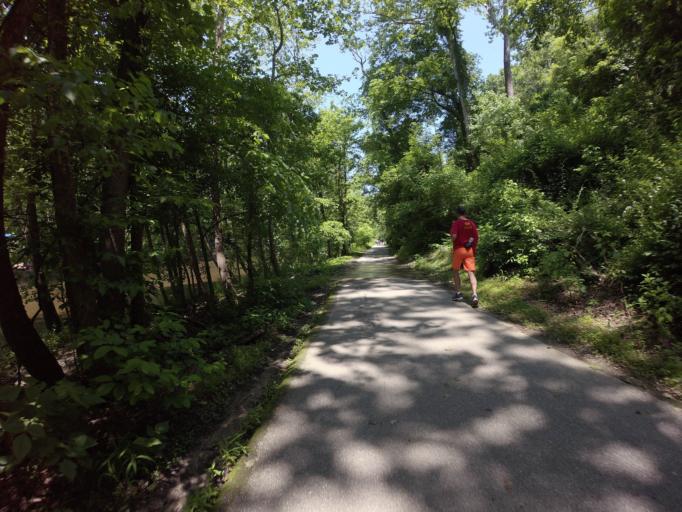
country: US
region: Maryland
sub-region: Howard County
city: Ilchester
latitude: 39.2427
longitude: -76.7504
